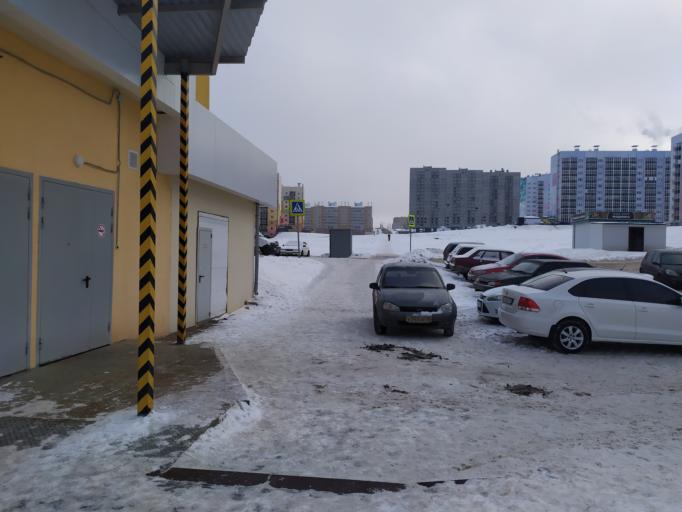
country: RU
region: Chuvashia
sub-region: Cheboksarskiy Rayon
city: Cheboksary
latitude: 56.1188
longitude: 47.2077
